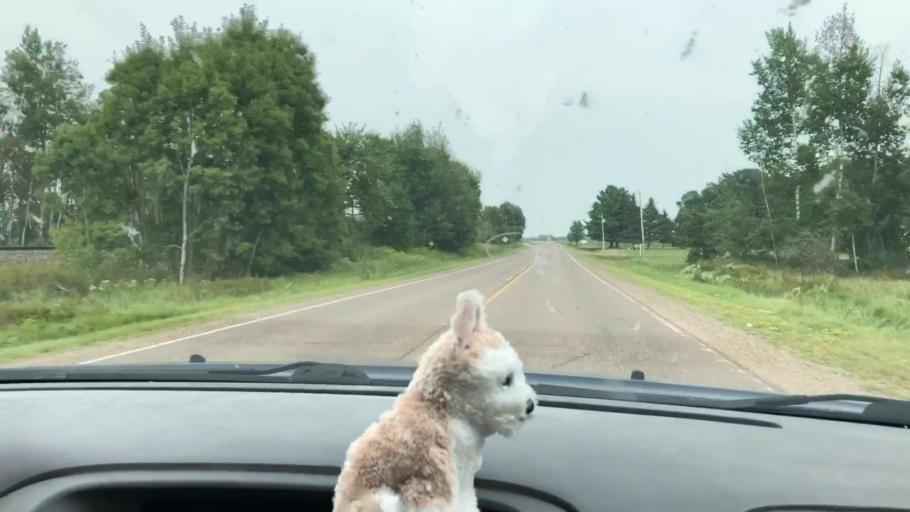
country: US
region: Wisconsin
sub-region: Chippewa County
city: Stanley
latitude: 44.9576
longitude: -90.9013
